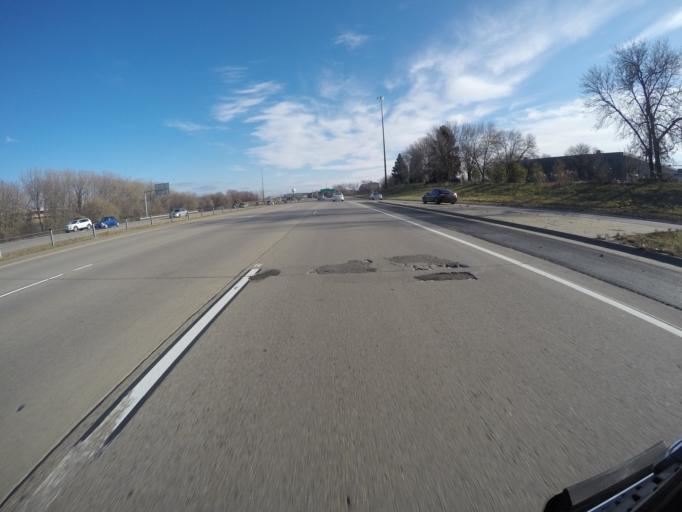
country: US
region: Minnesota
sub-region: Hennepin County
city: Eden Prairie
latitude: 44.8614
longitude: -93.4554
